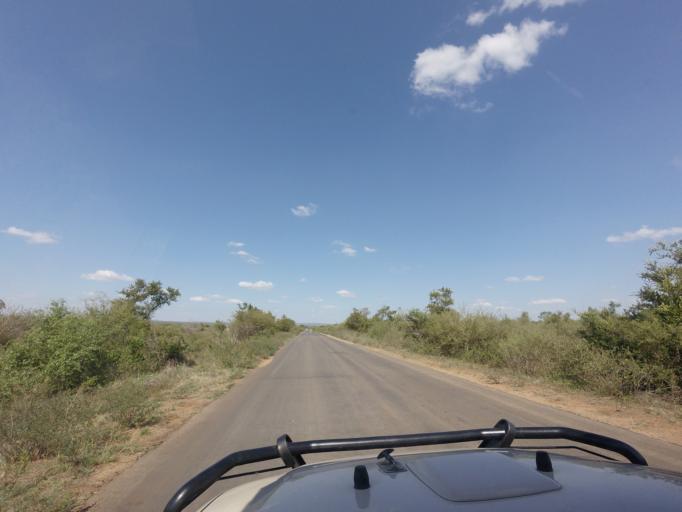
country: ZA
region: Mpumalanga
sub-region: Ehlanzeni District
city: Komatipoort
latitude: -25.1249
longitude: 31.9188
